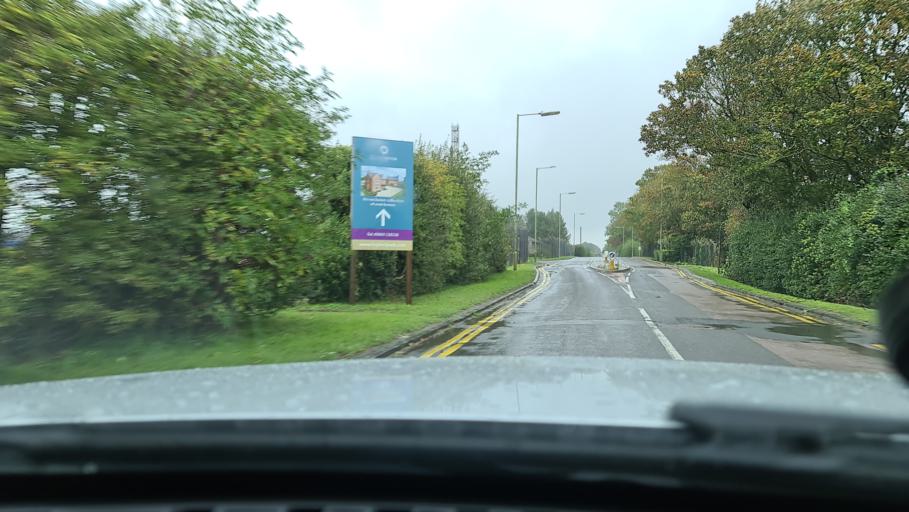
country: GB
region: England
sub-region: Oxfordshire
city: Somerton
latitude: 51.9296
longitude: -1.2708
